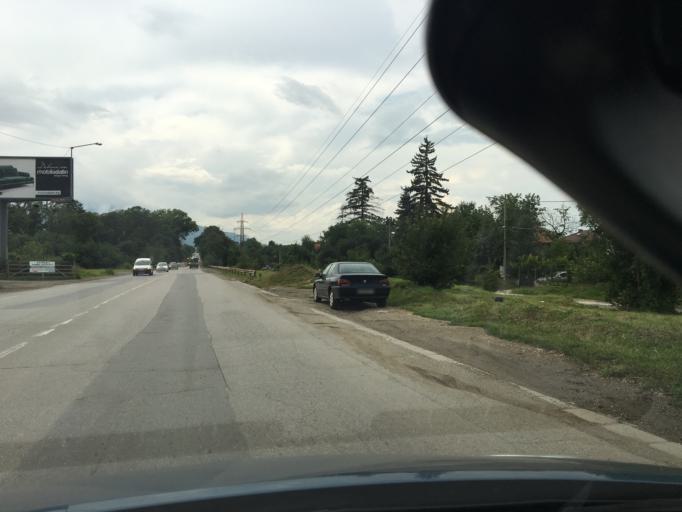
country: BG
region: Sofia-Capital
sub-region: Stolichna Obshtina
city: Sofia
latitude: 42.6225
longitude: 23.4040
